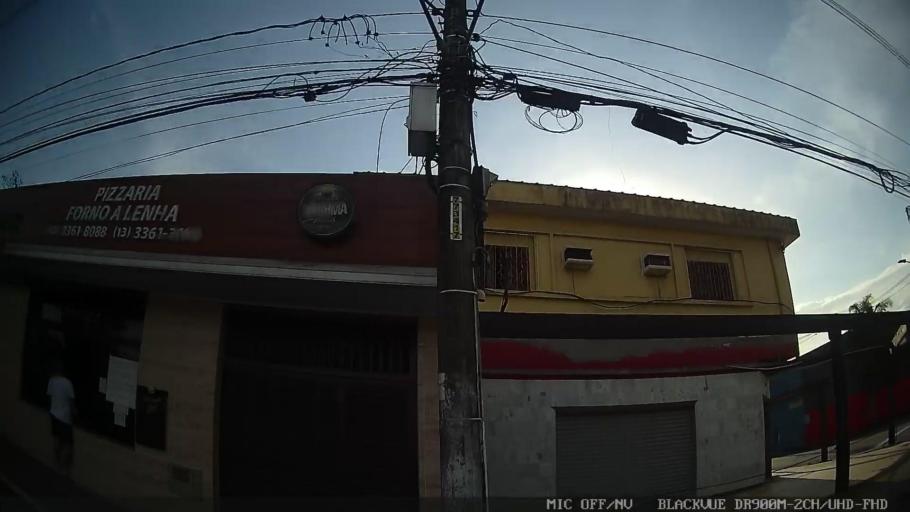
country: BR
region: Sao Paulo
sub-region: Cubatao
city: Cubatao
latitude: -23.8969
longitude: -46.4217
